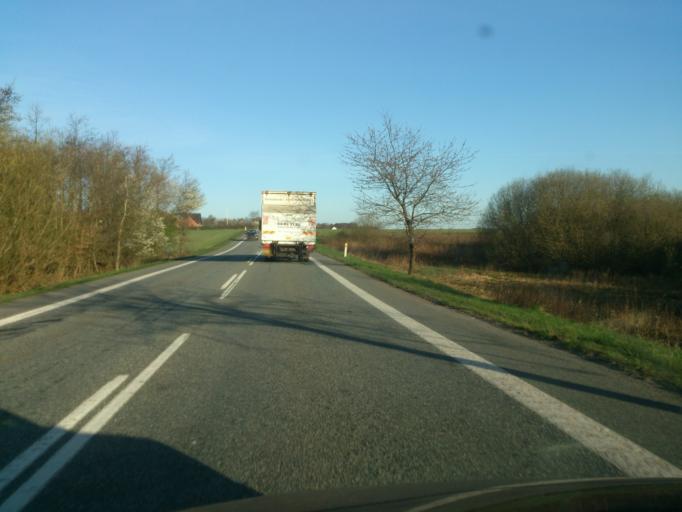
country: DK
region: Central Jutland
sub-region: Favrskov Kommune
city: Ulstrup
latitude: 56.4477
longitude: 9.7351
